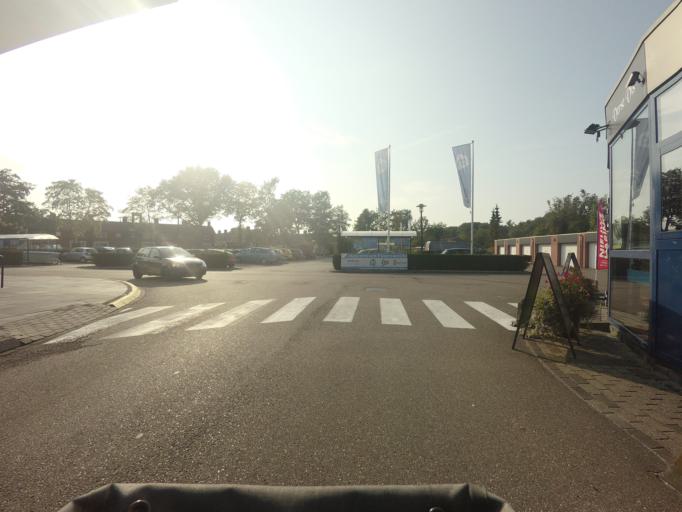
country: NL
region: Groningen
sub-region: Gemeente Haren
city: Haren
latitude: 53.1474
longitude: 6.5657
